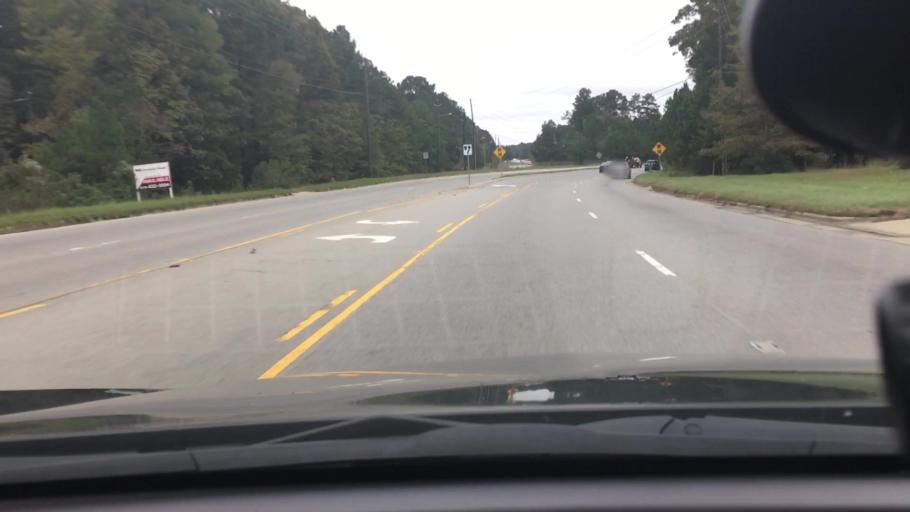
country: US
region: North Carolina
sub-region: Wake County
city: Apex
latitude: 35.6979
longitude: -78.8337
